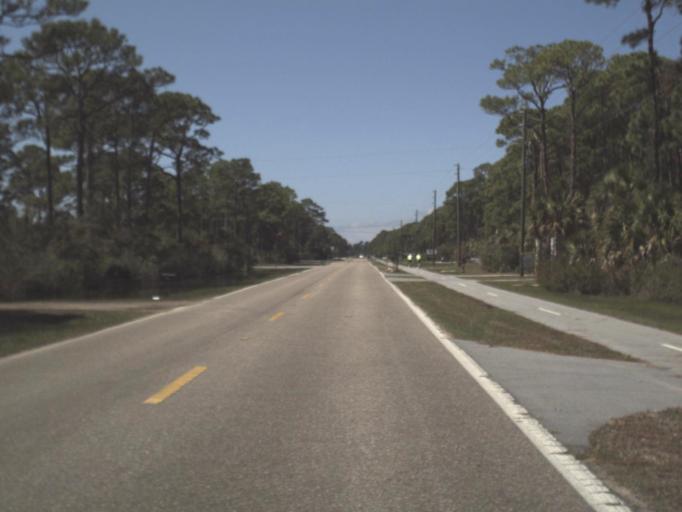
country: US
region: Florida
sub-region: Gulf County
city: Port Saint Joe
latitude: 29.6836
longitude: -85.3261
